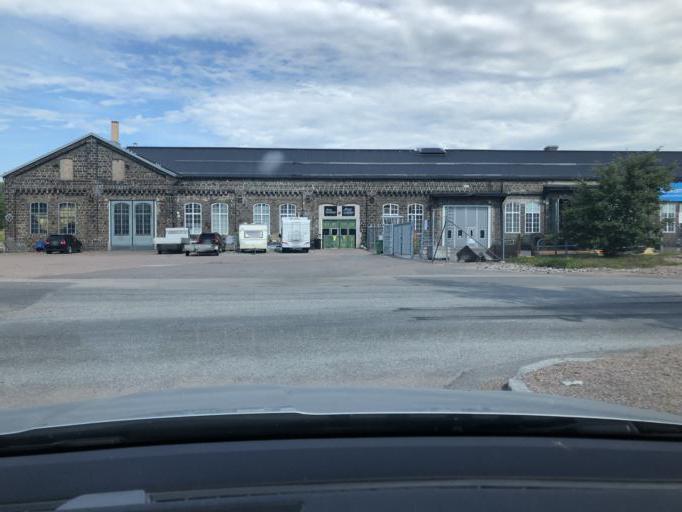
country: SE
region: Dalarna
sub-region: Avesta Kommun
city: Avesta
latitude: 60.1478
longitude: 16.1756
